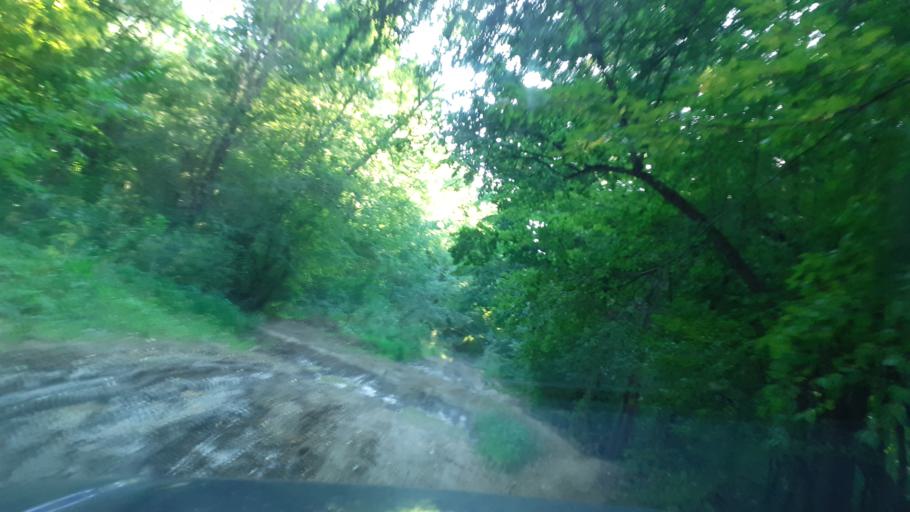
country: RU
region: Krasnodarskiy
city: Chernomorskiy
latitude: 44.6617
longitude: 38.4690
